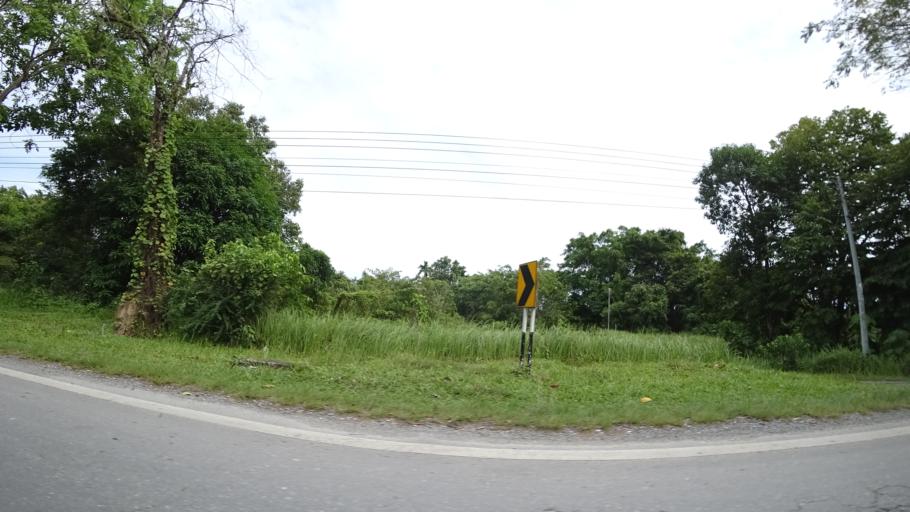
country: MY
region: Sarawak
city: Limbang
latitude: 4.7460
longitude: 115.0046
